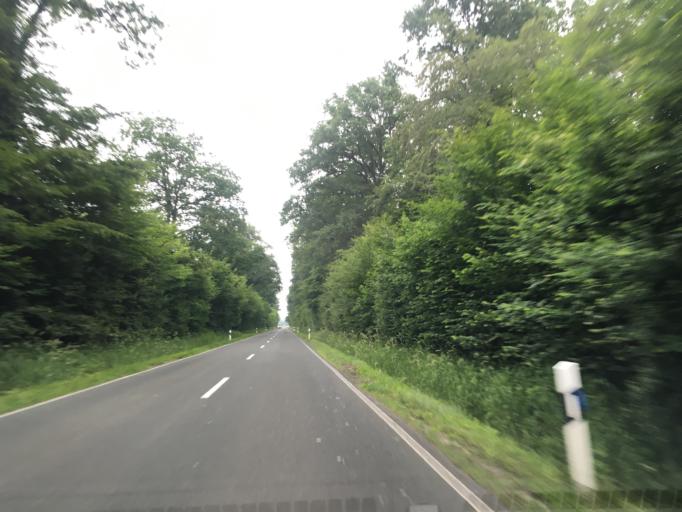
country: DE
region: North Rhine-Westphalia
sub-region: Regierungsbezirk Munster
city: Laer
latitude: 52.0903
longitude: 7.3454
